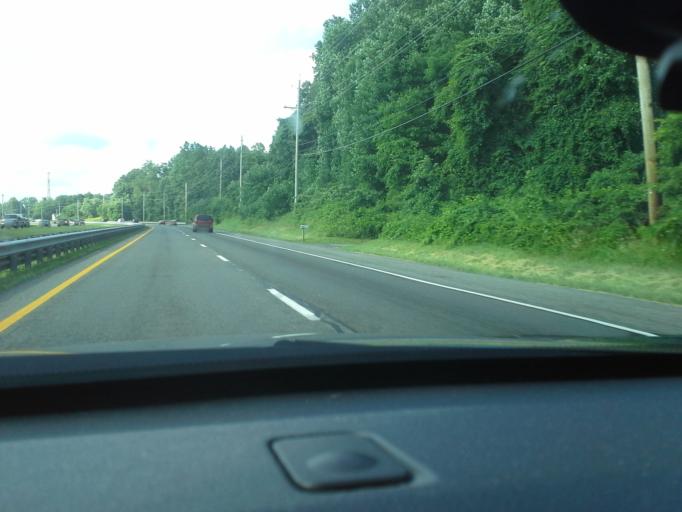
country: US
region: Maryland
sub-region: Calvert County
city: Prince Frederick
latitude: 38.5748
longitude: -76.6019
